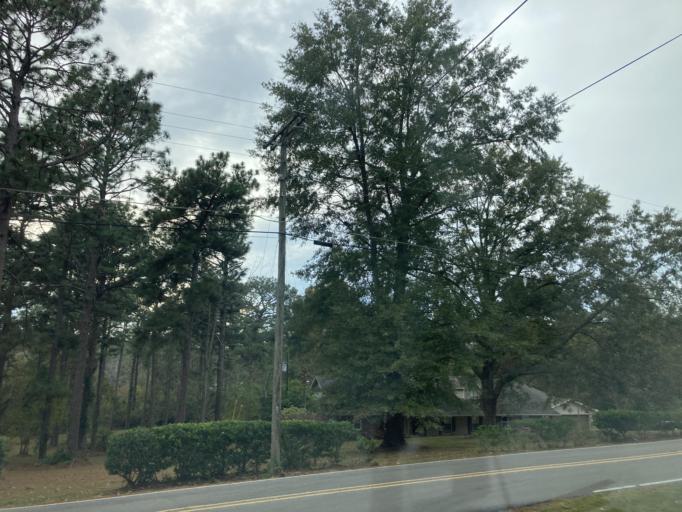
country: US
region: Mississippi
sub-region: Lamar County
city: West Hattiesburg
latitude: 31.3098
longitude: -89.4384
